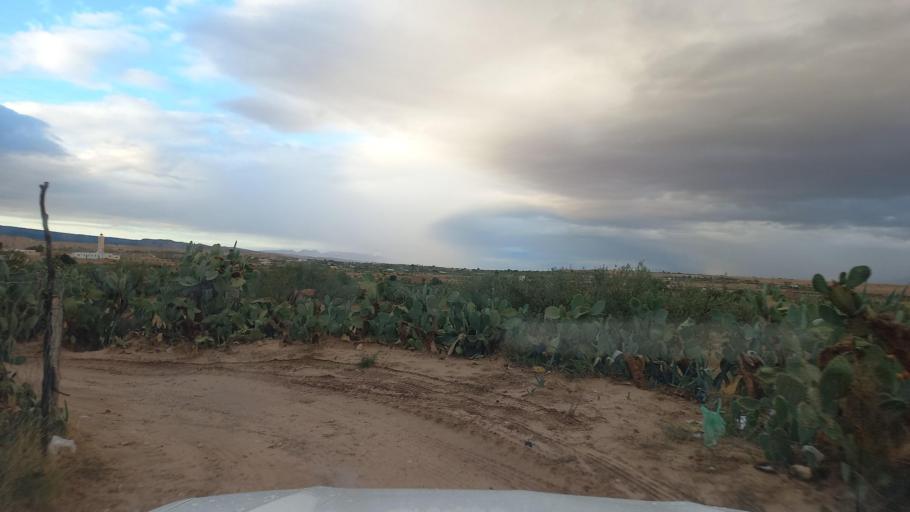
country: TN
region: Al Qasrayn
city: Kasserine
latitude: 35.2599
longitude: 8.9352
